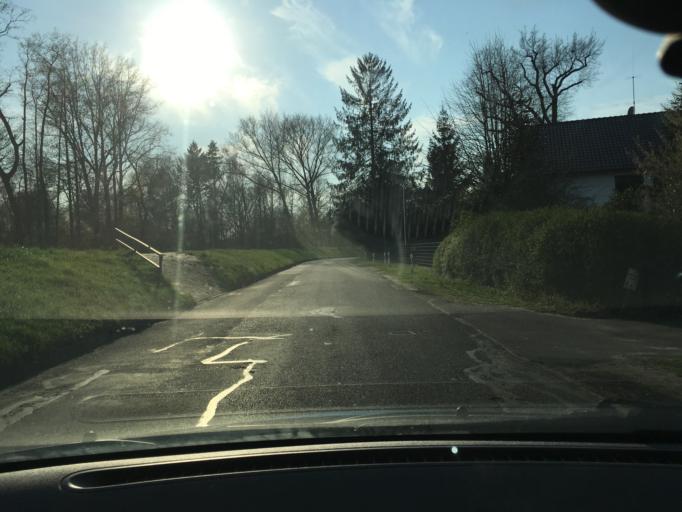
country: DE
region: Lower Saxony
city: Stelle
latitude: 53.4110
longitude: 10.0596
